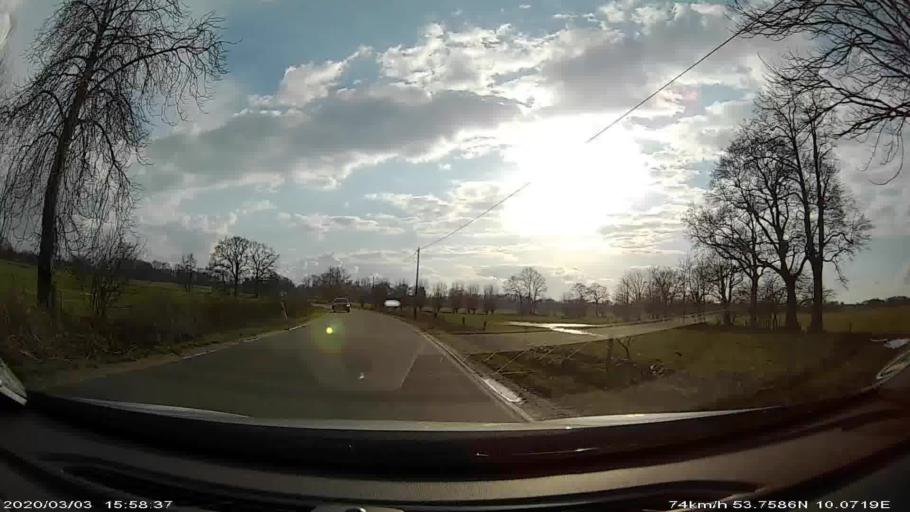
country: DE
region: Schleswig-Holstein
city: Tangstedt
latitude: 53.7596
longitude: 10.0746
